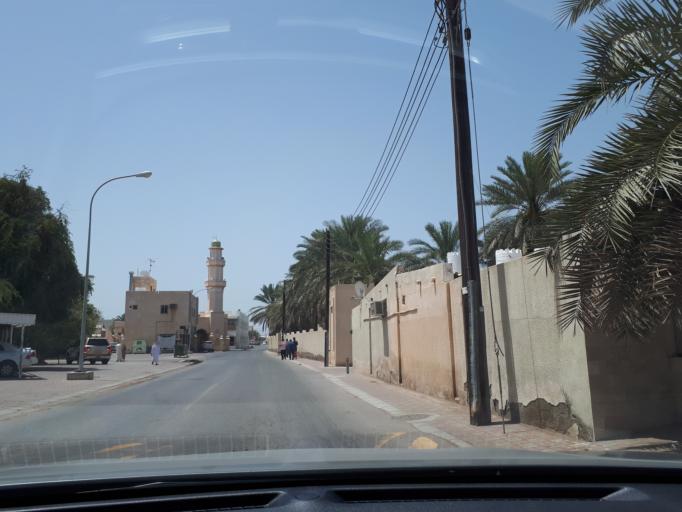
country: OM
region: Muhafazat Masqat
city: As Sib al Jadidah
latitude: 23.6791
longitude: 58.1276
